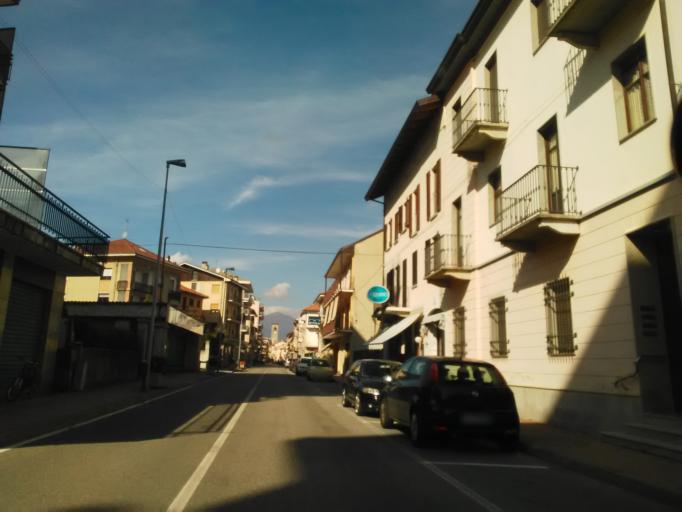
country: IT
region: Piedmont
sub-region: Provincia di Vercelli
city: Serravalle Sesia
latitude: 45.6832
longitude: 8.3143
